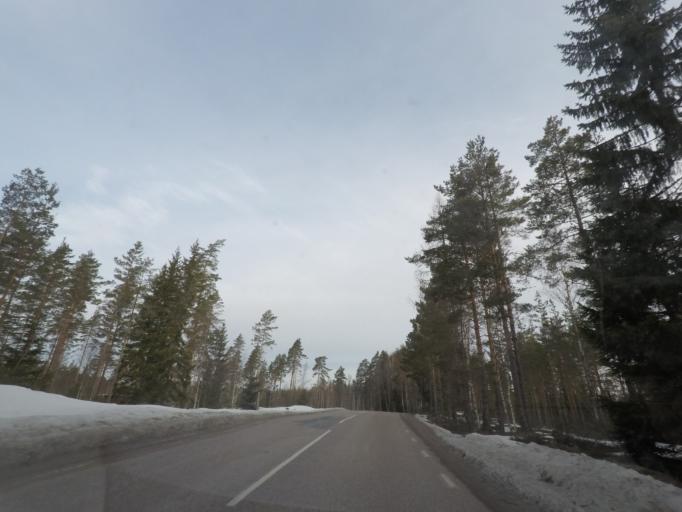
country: SE
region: Vaestmanland
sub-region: Surahammars Kommun
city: Surahammar
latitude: 59.7627
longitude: 16.2934
